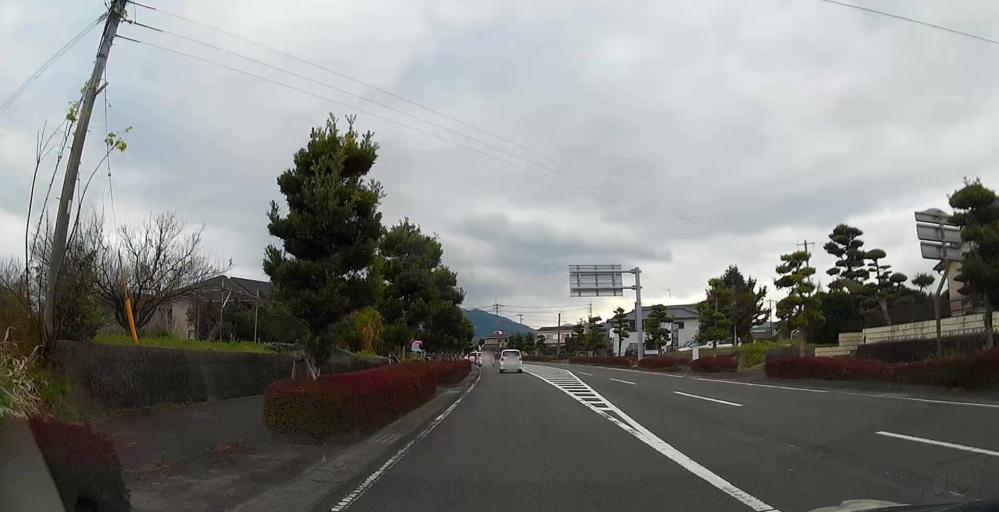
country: JP
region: Kagoshima
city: Izumi
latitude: 32.0820
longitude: 130.3444
